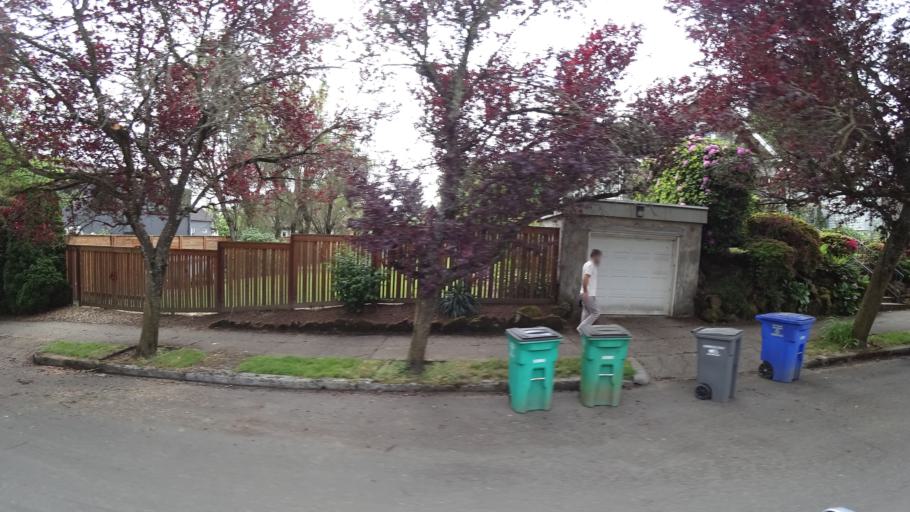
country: US
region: Oregon
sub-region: Multnomah County
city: Portland
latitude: 45.5535
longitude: -122.6557
